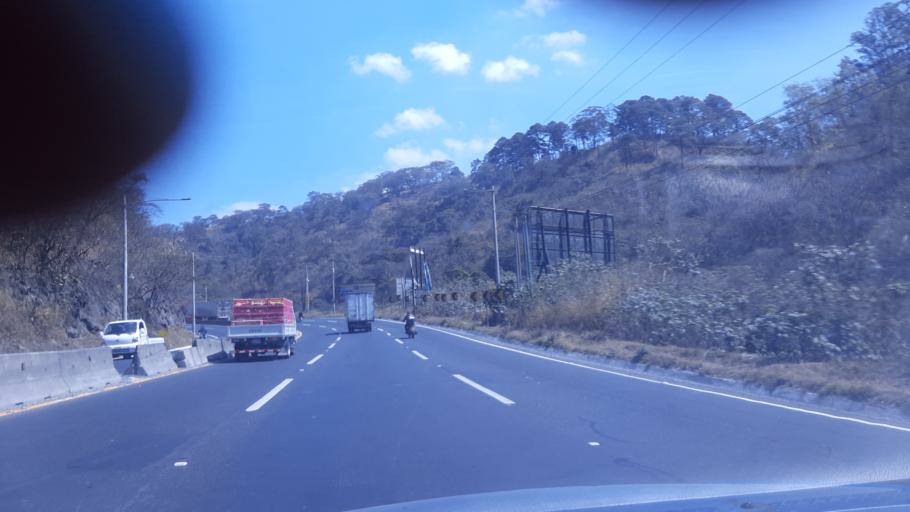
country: GT
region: Guatemala
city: Amatitlan
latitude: 14.5007
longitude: -90.6279
